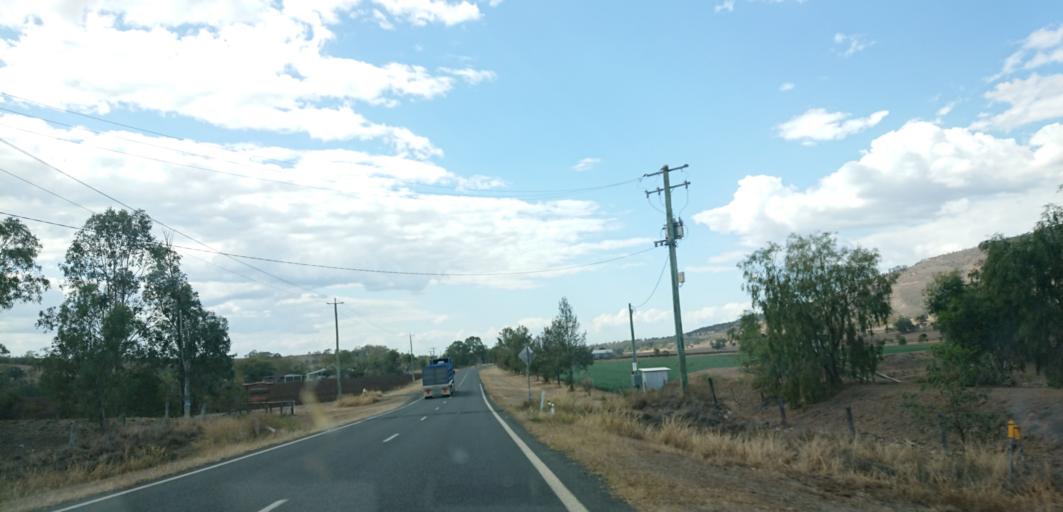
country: AU
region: Queensland
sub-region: Lockyer Valley
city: Gatton
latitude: -27.6558
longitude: 152.1679
